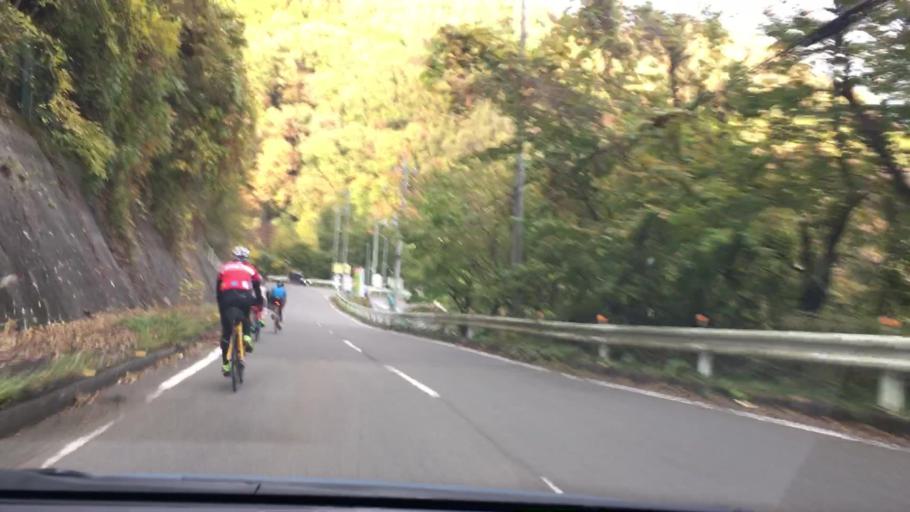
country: JP
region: Yamanashi
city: Uenohara
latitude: 35.5491
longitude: 139.1342
